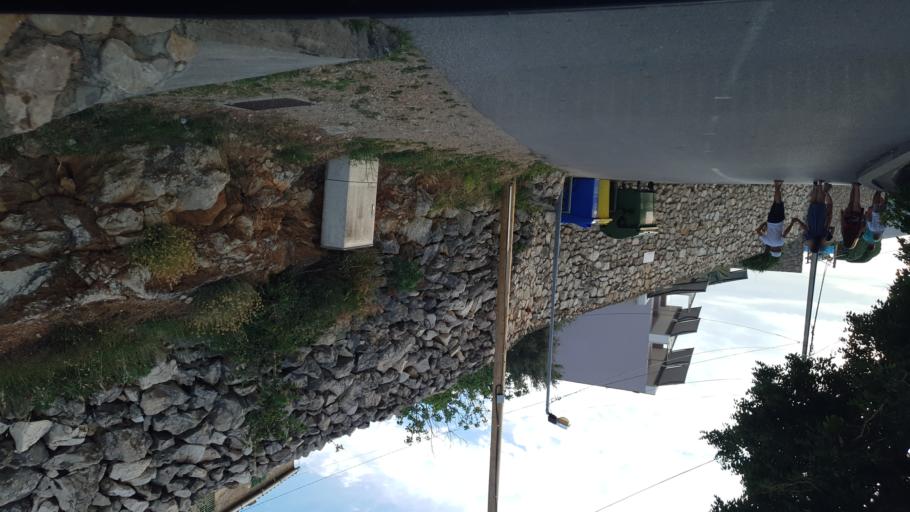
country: HR
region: Primorsko-Goranska
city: Punat
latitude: 44.9573
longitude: 14.6895
